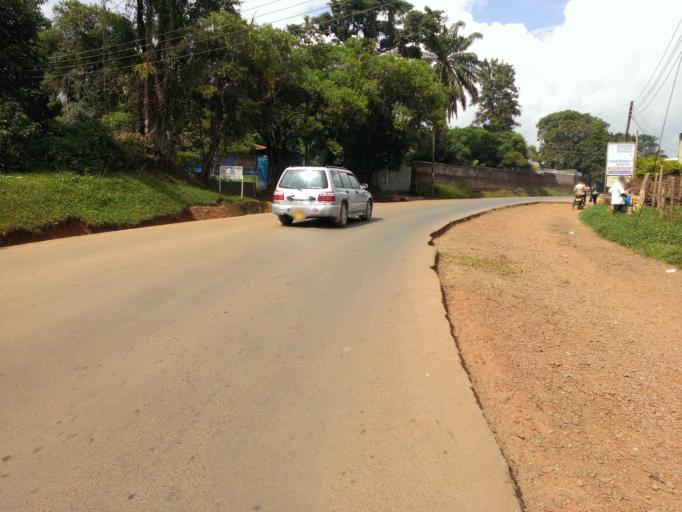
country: UG
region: Central Region
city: Kampala Central Division
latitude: 0.3222
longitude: 32.5597
